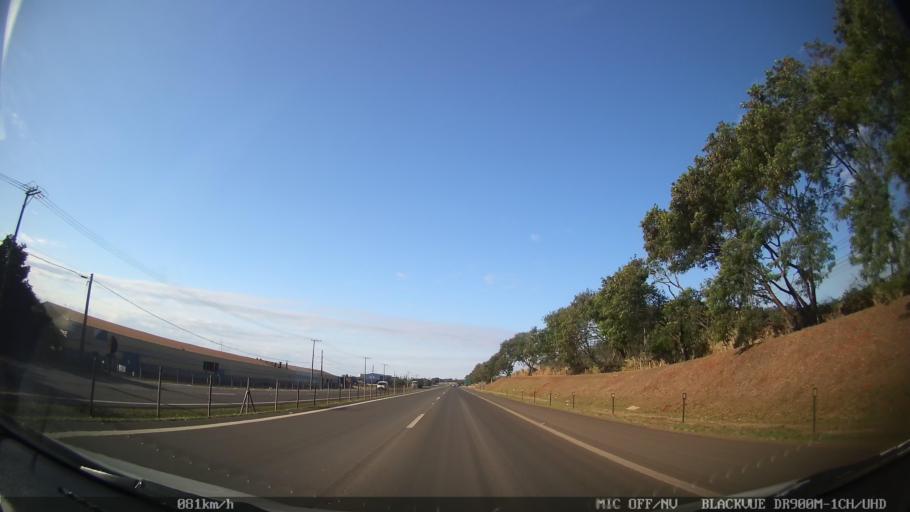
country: BR
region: Sao Paulo
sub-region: Piracicaba
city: Piracicaba
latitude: -22.6669
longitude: -47.6218
